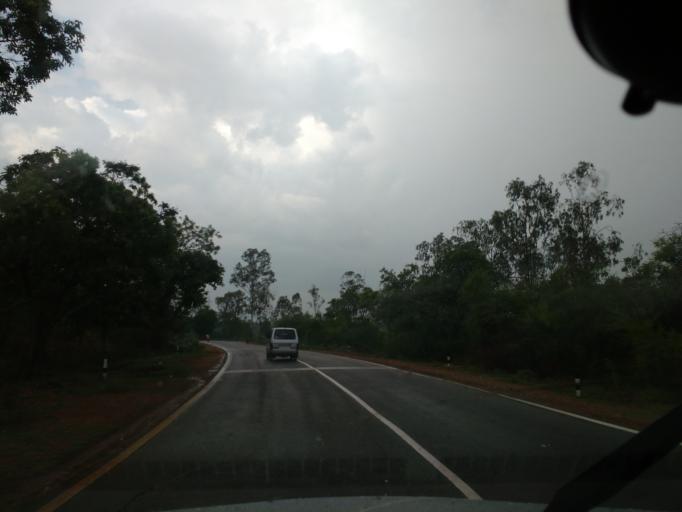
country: IN
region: Karnataka
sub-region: Tumkur
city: Tiptur
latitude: 13.2977
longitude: 76.5900
